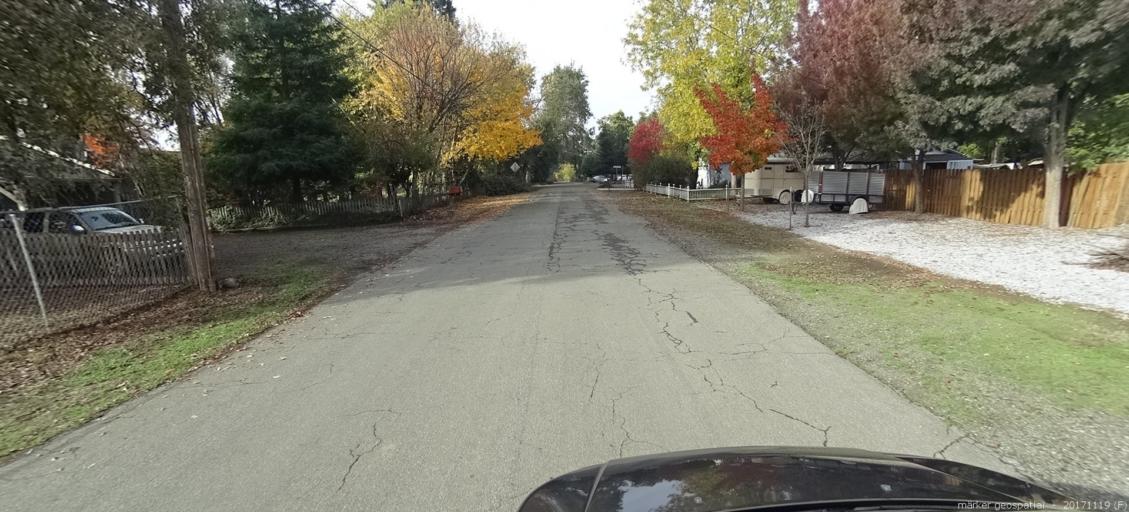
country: US
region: California
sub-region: Shasta County
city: Anderson
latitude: 40.5148
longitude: -122.3481
